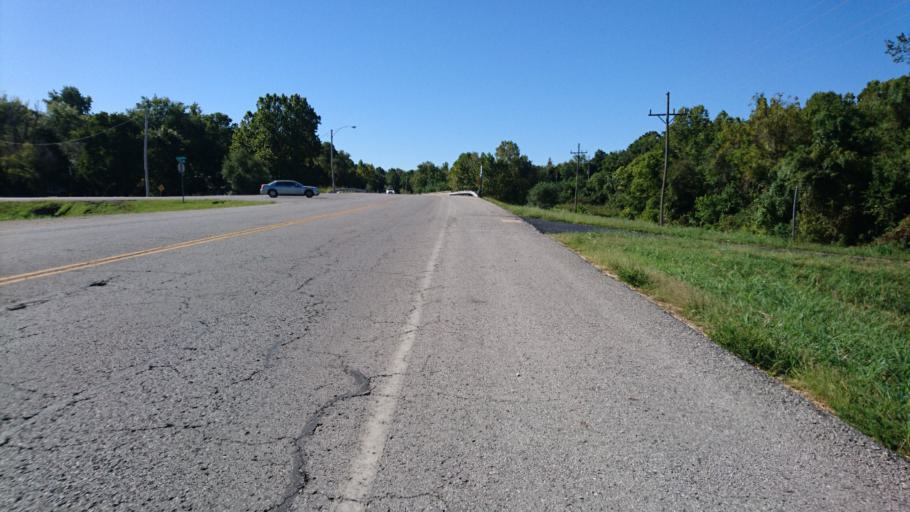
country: US
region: Missouri
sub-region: Jasper County
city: Joplin
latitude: 37.1026
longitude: -94.4947
